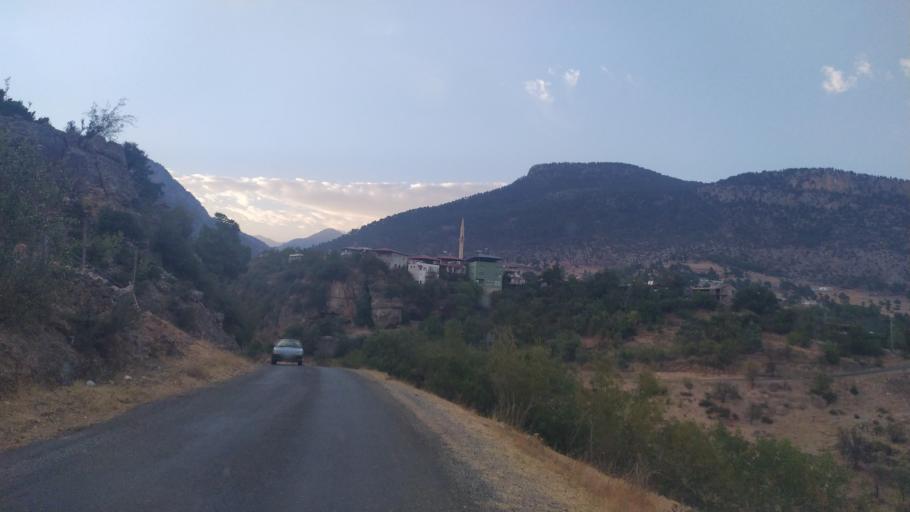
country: TR
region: Mersin
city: Camliyayla
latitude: 37.2368
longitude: 34.7176
